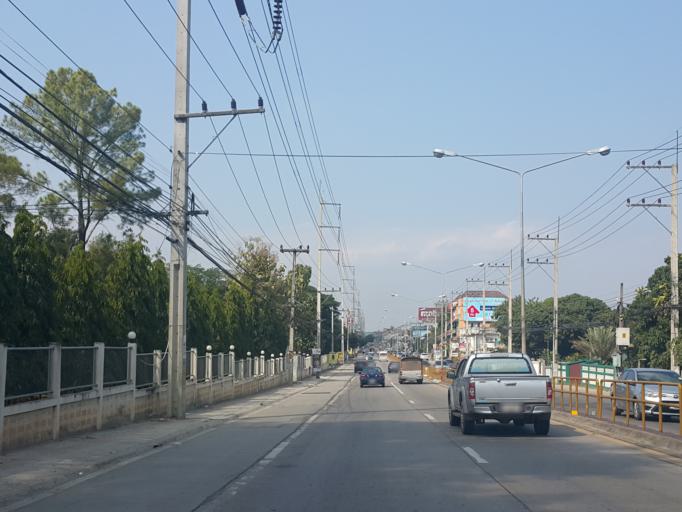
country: TH
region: Chiang Mai
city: San Sai
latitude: 18.8936
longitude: 98.9528
